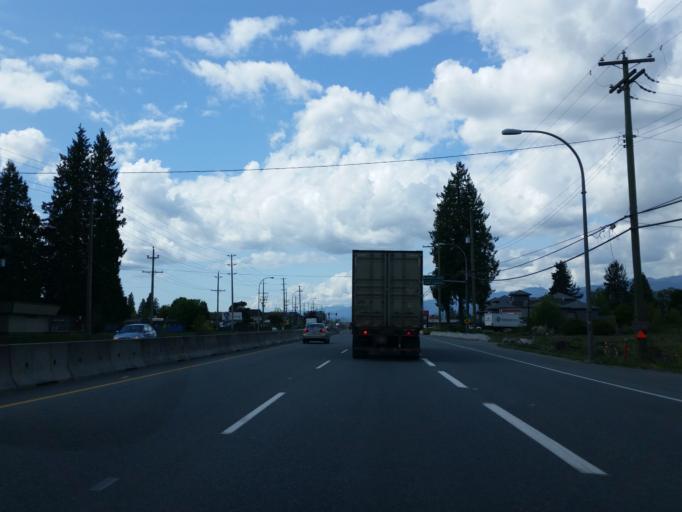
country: CA
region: British Columbia
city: Pitt Meadows
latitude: 49.2295
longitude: -122.6852
